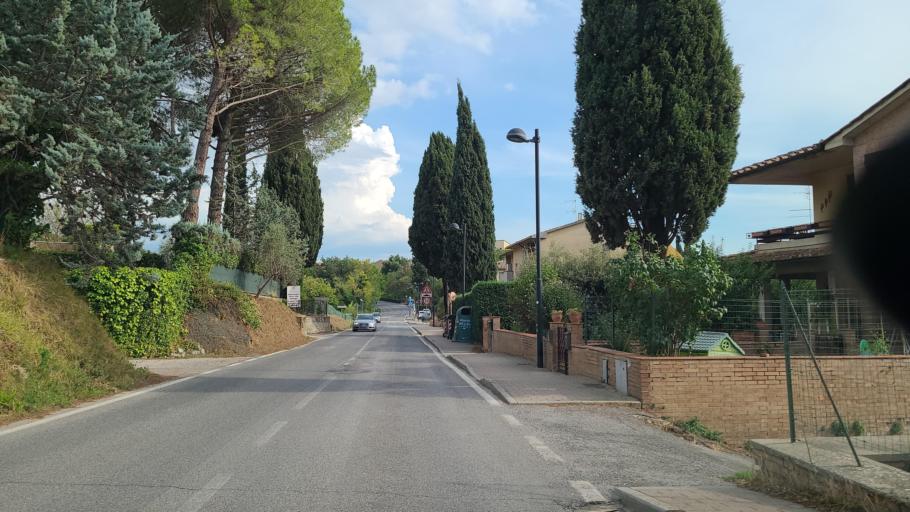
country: IT
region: Tuscany
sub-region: Provincia di Siena
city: San Gimignano
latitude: 43.4737
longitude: 11.0315
